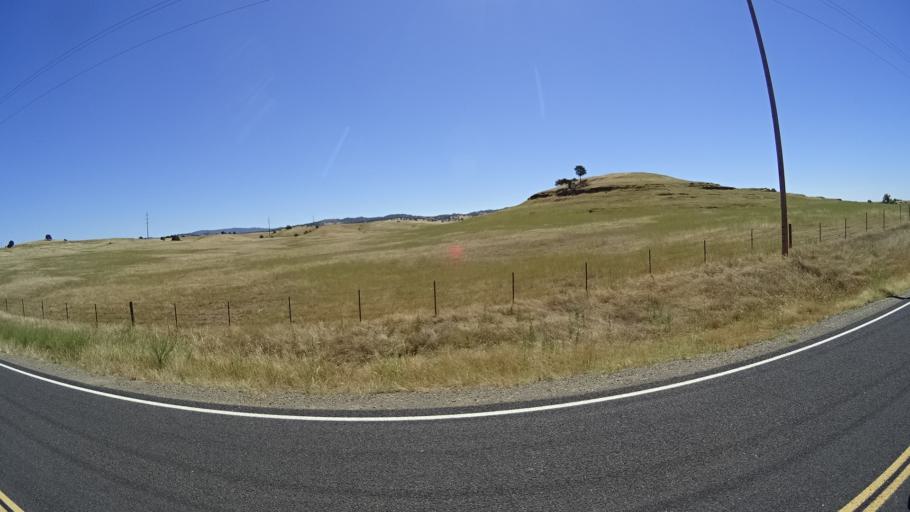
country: US
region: California
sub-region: Calaveras County
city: Rancho Calaveras
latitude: 38.0573
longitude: -120.8713
